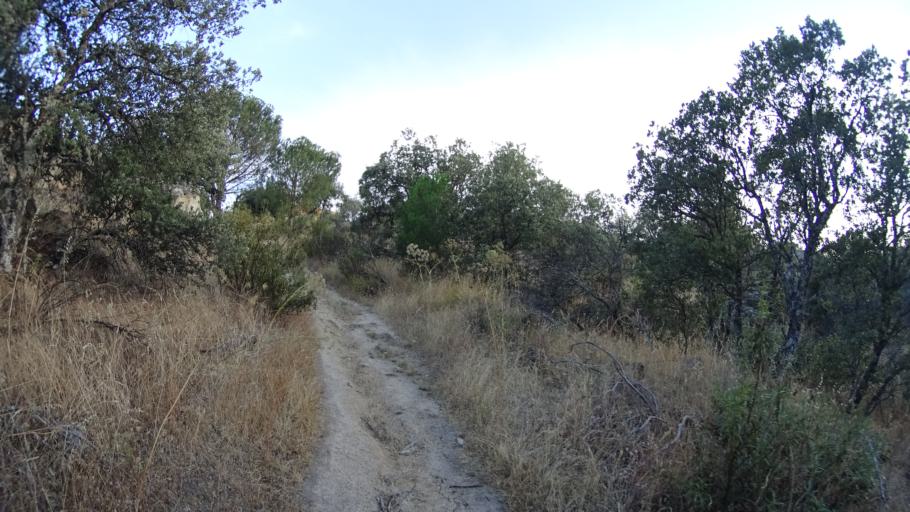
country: ES
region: Madrid
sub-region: Provincia de Madrid
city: Torrelodones
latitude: 40.5908
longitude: -3.9456
